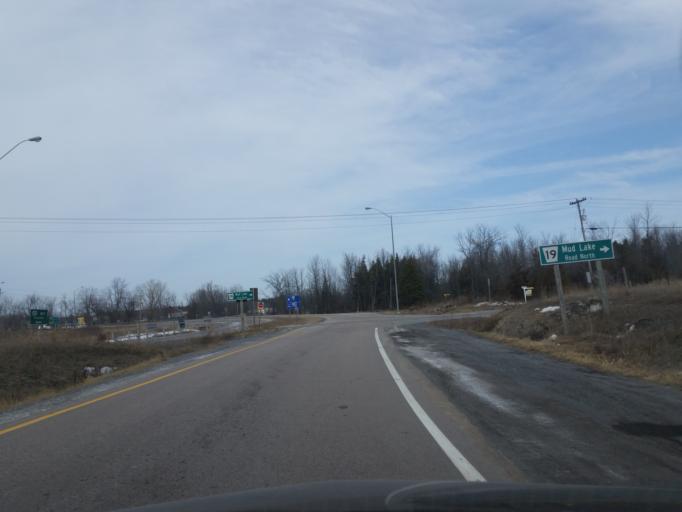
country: CA
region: Ontario
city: Skatepark
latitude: 44.2832
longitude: -76.7144
